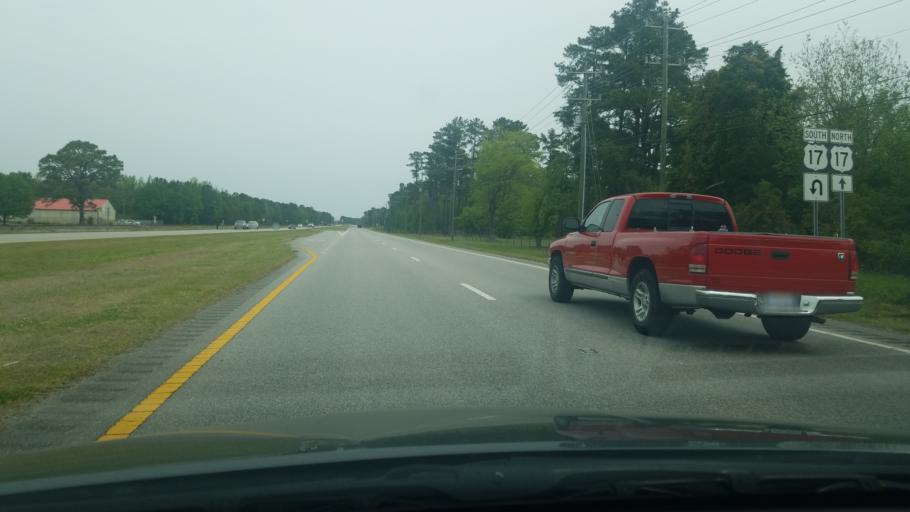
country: US
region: North Carolina
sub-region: Beaufort County
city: Washington
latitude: 35.4572
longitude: -77.1217
